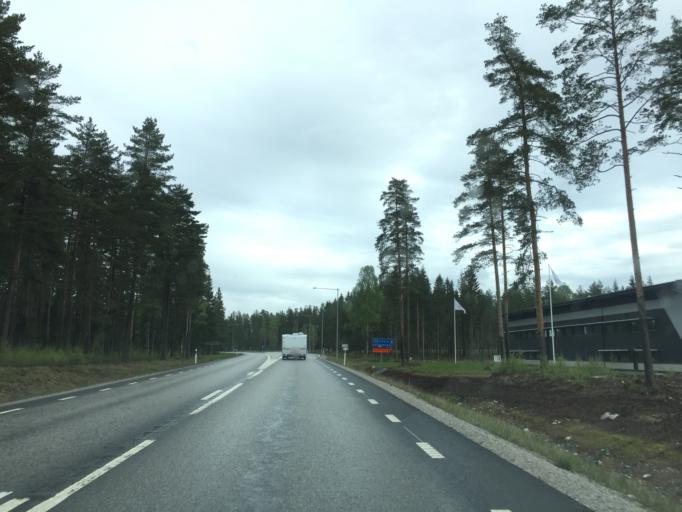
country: SE
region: OErebro
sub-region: Lindesbergs Kommun
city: Lindesberg
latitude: 59.6152
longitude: 15.1875
